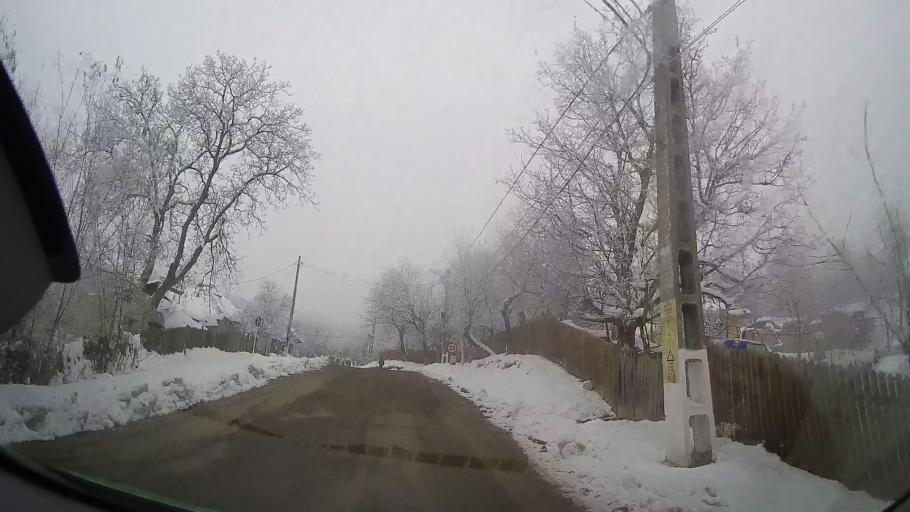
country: RO
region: Iasi
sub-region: Comuna Tansa
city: Tansa
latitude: 46.9094
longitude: 27.2386
